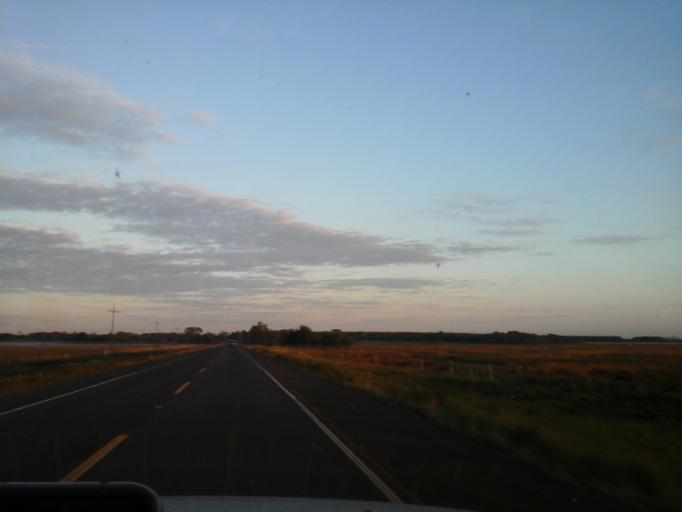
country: PY
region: Itapua
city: General Delgado
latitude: -27.0799
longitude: -56.5664
